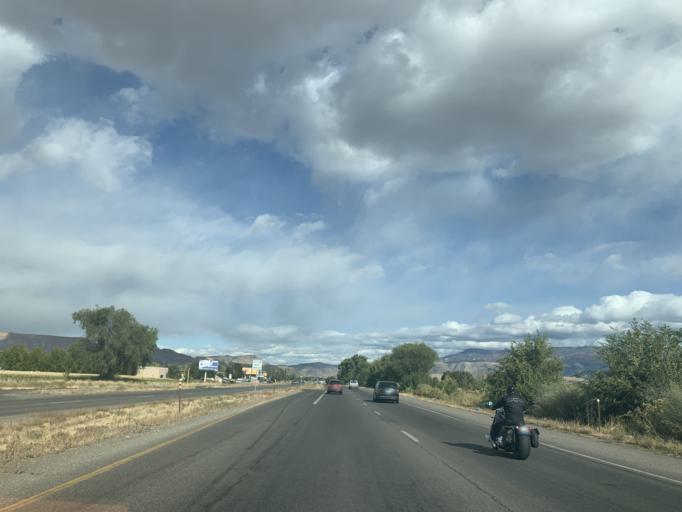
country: US
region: Colorado
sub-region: Mesa County
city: Fruitvale
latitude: 39.0797
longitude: -108.4852
